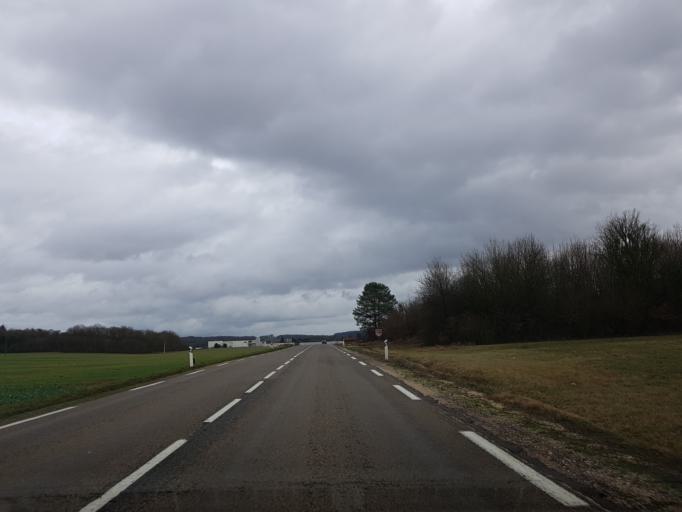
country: FR
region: Franche-Comte
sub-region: Departement de la Haute-Saone
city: Jussey
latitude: 47.7176
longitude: 5.8752
